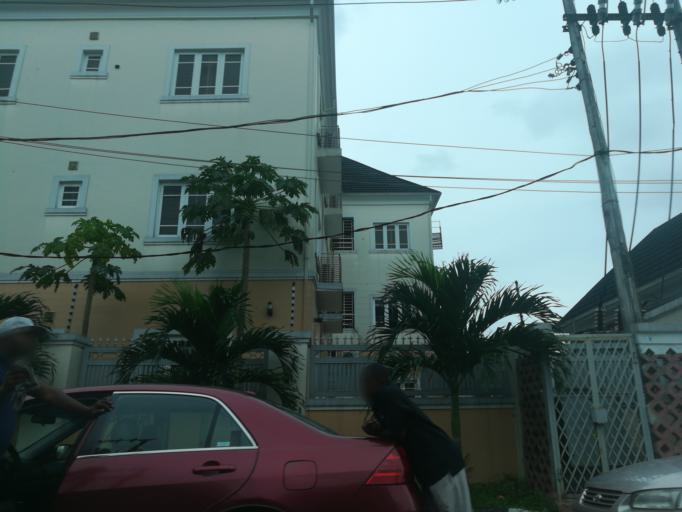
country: NG
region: Rivers
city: Port Harcourt
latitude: 4.8238
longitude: 6.9902
